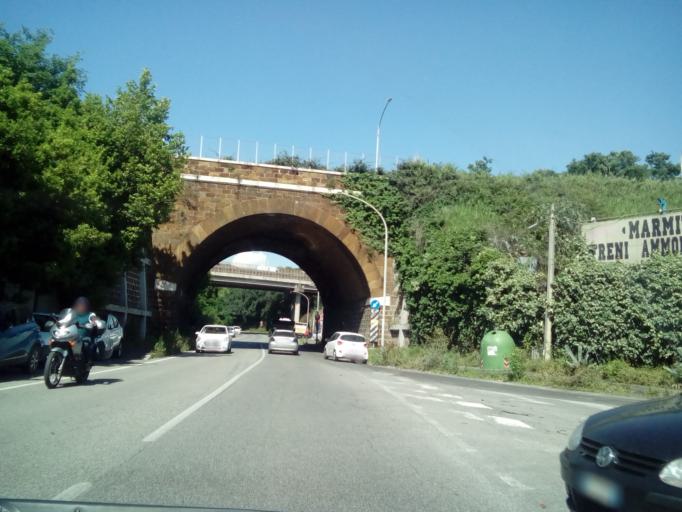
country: VA
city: Vatican City
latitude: 41.8421
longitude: 12.4671
